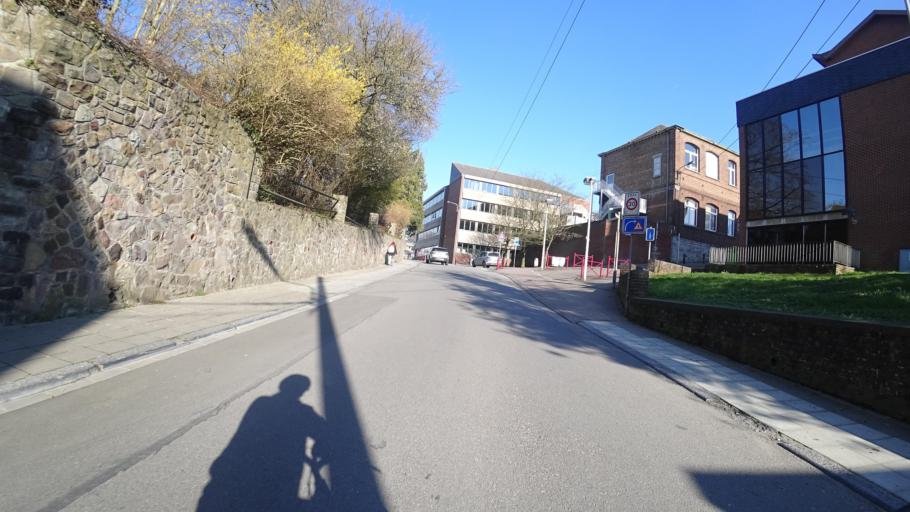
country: BE
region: Wallonia
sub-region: Province de Namur
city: Gembloux
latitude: 50.5592
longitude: 4.6938
